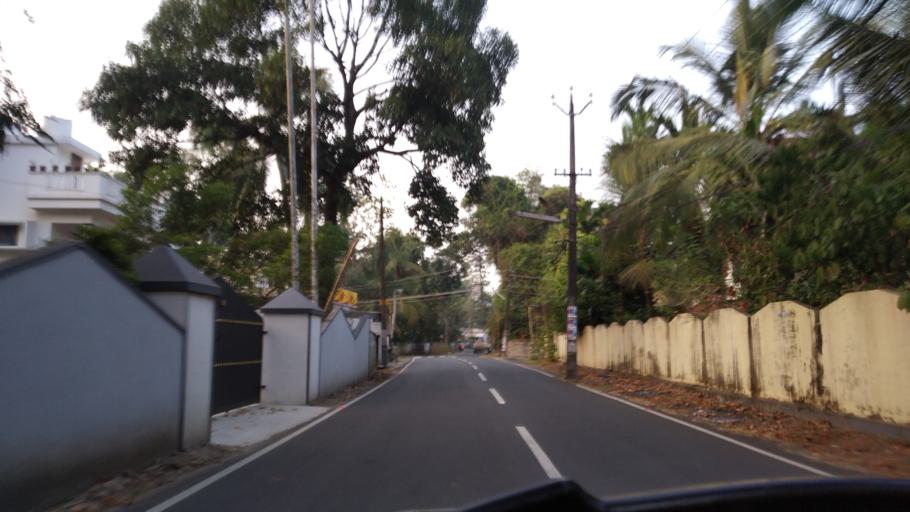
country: IN
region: Kerala
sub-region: Ernakulam
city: Elur
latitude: 10.1132
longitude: 76.2434
